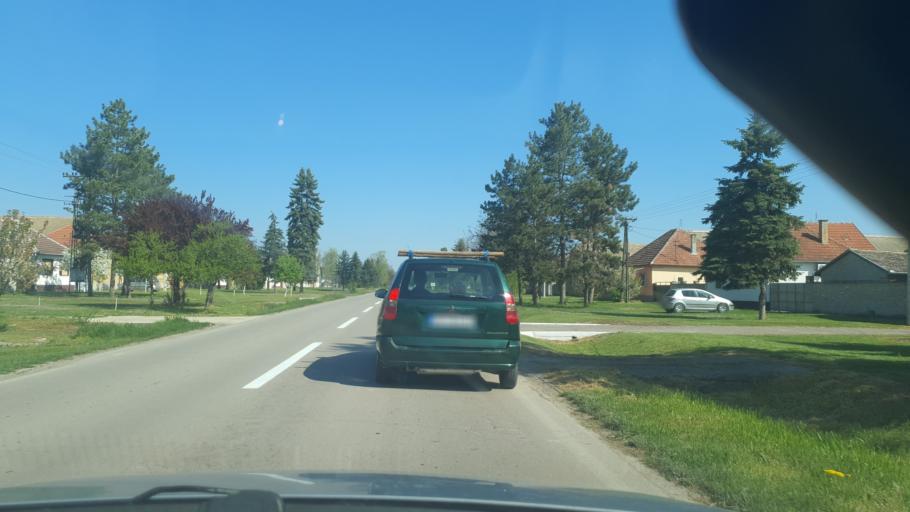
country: RS
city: Kolut
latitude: 45.8490
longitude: 18.9338
